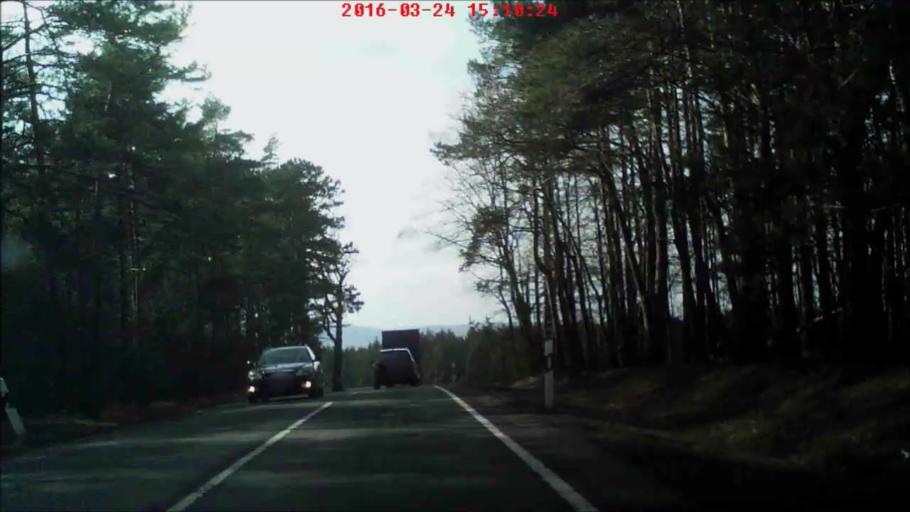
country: DE
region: Thuringia
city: Stadtilm
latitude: 50.7673
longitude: 11.1066
